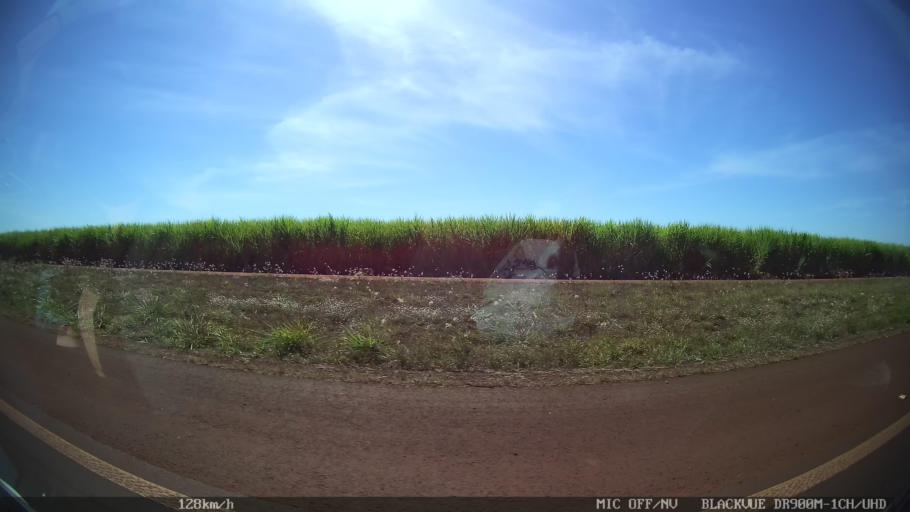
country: BR
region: Sao Paulo
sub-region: Guaira
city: Guaira
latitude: -20.4437
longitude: -48.3449
